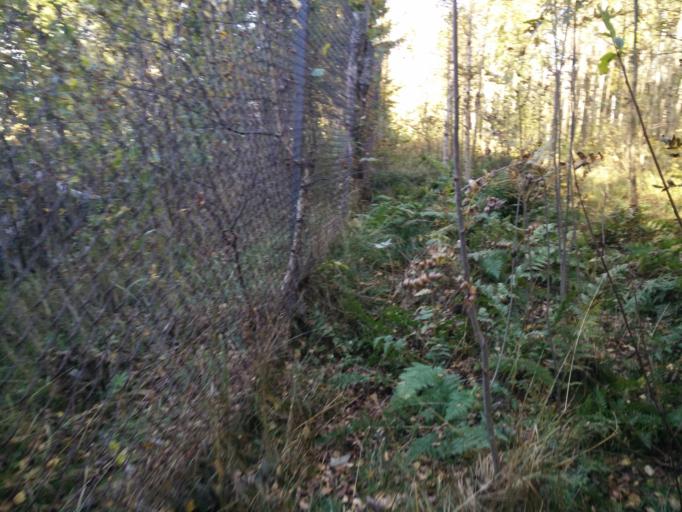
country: SE
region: Vaesternorrland
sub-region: Haernoesands Kommun
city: Haernoesand
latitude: 62.6412
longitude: 17.9696
